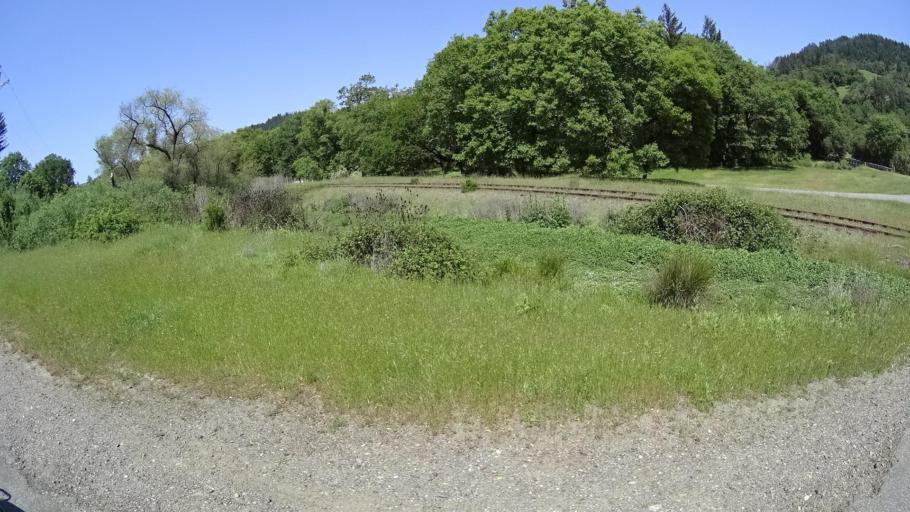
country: US
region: California
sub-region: Humboldt County
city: Redway
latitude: 40.2164
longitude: -123.6349
